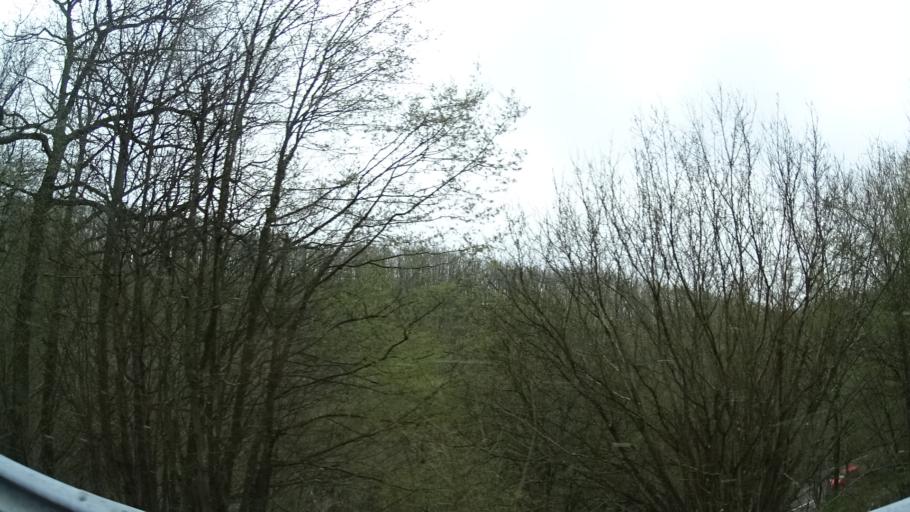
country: DE
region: Rheinland-Pfalz
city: Vollmersbach
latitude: 49.7323
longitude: 7.3180
